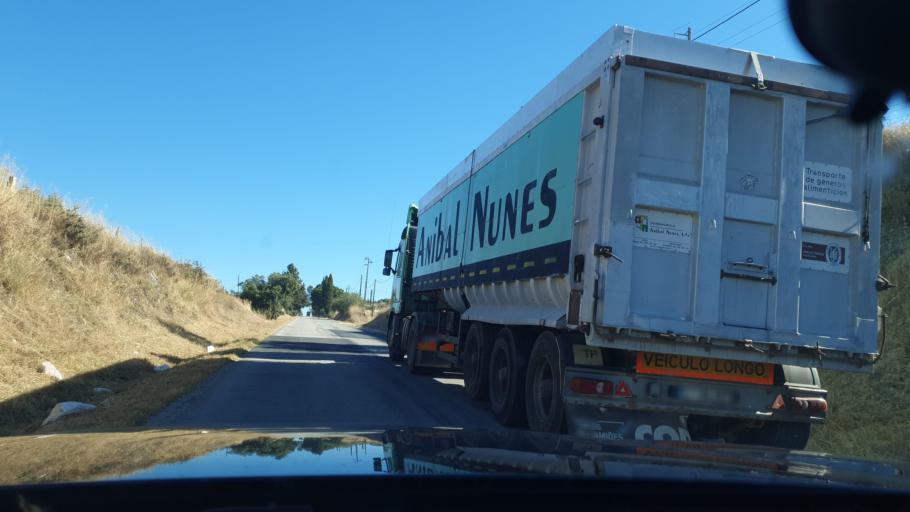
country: PT
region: Evora
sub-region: Alandroal
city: Alandroal
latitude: 38.7189
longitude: -7.4063
